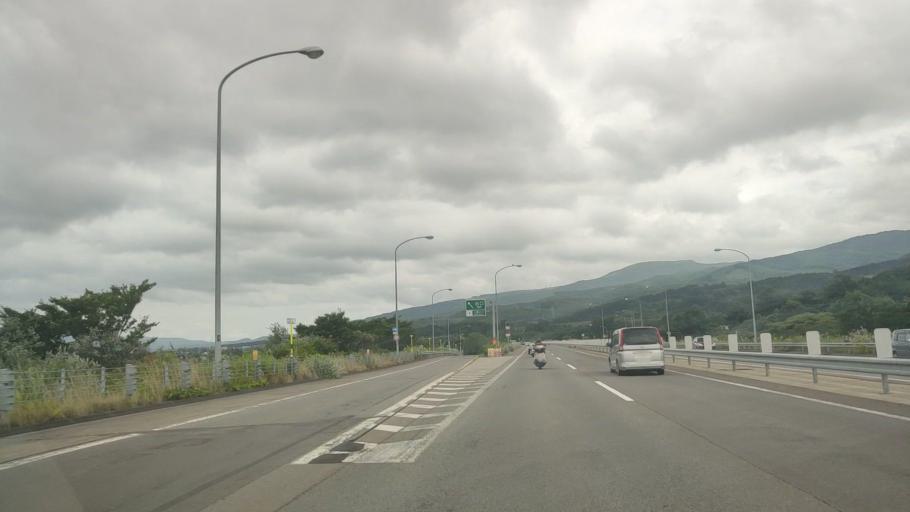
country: JP
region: Hokkaido
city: Nanae
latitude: 41.8657
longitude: 140.7303
